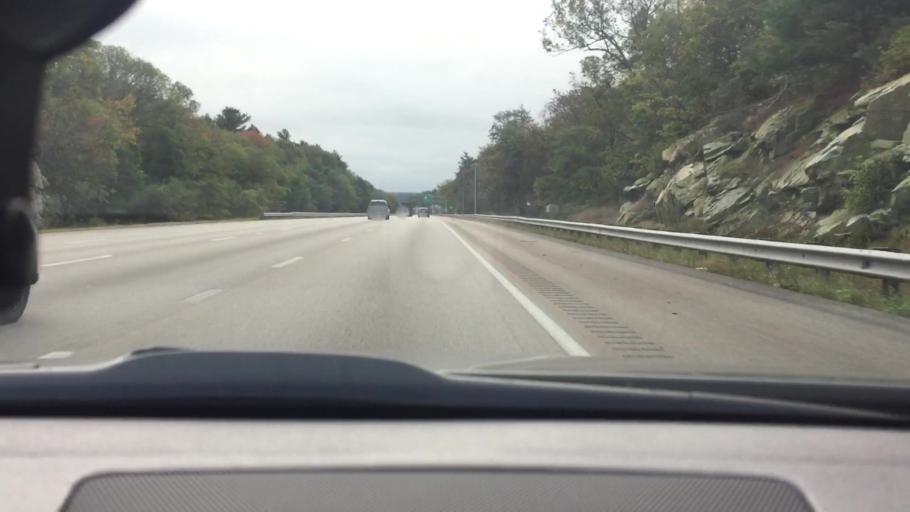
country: US
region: Massachusetts
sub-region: Norfolk County
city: Dedham
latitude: 42.2371
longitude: -71.1982
